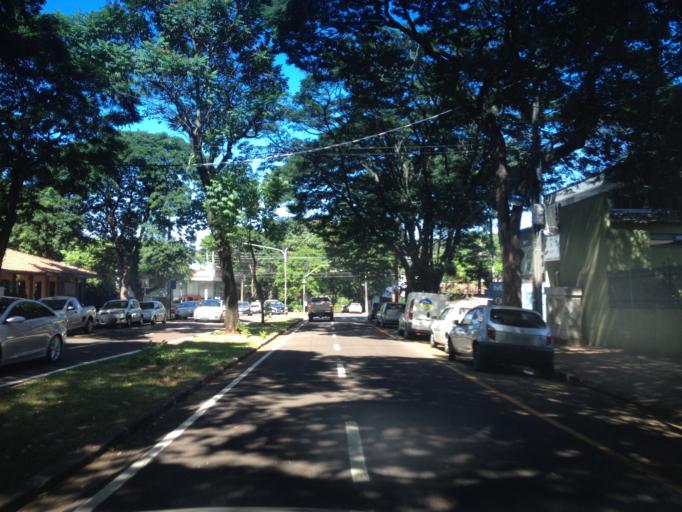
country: BR
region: Parana
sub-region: Maringa
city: Maringa
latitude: -23.4248
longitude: -51.9454
